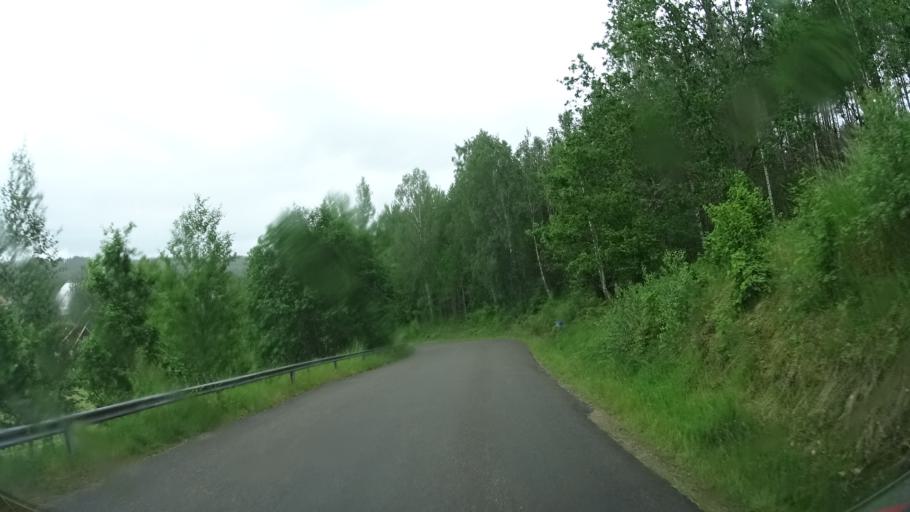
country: SE
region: Joenkoeping
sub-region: Eksjo Kommun
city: Mariannelund
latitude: 57.6768
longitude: 15.5863
